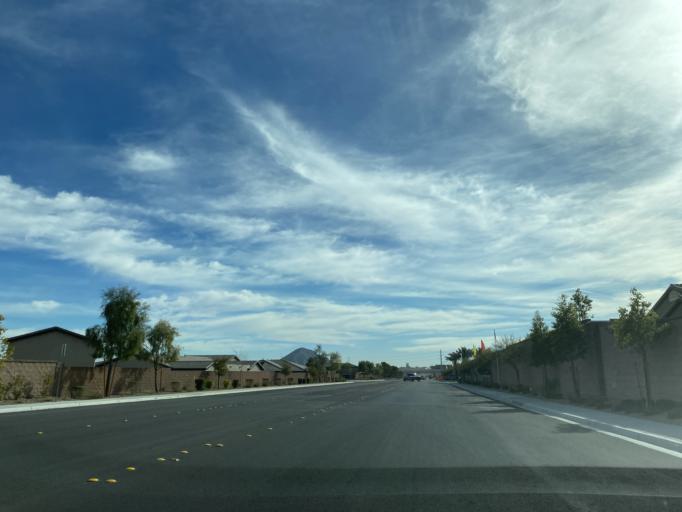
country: US
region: Nevada
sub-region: Clark County
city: Summerlin South
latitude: 36.2683
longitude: -115.3242
